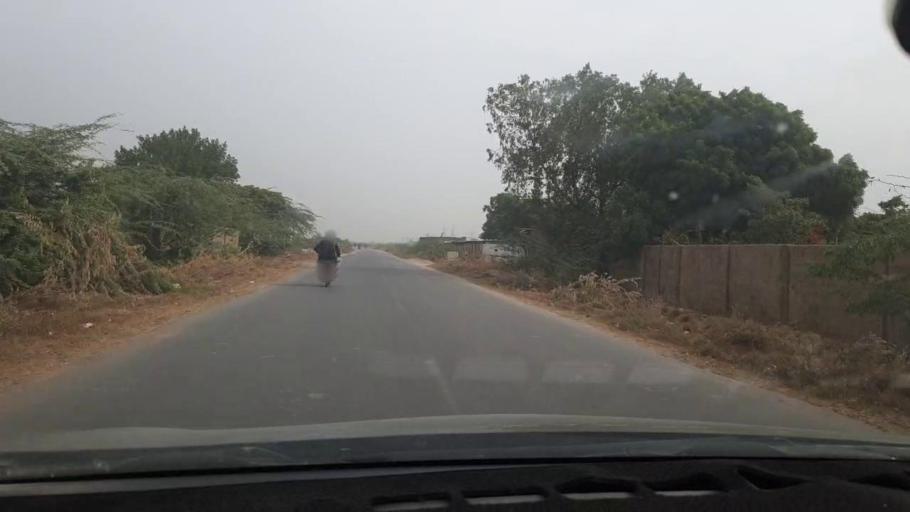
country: PK
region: Sindh
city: Malir Cantonment
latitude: 24.9139
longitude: 67.2713
